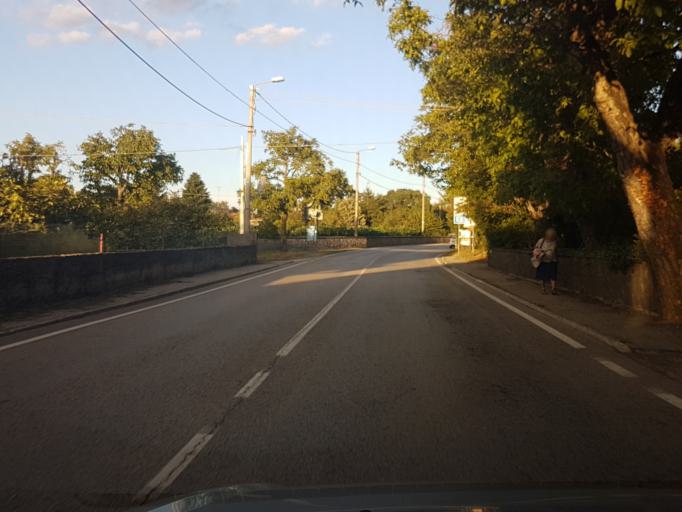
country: IT
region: Friuli Venezia Giulia
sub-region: Provincia di Trieste
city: Prosecco-Contovello
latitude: 45.7074
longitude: 13.7377
